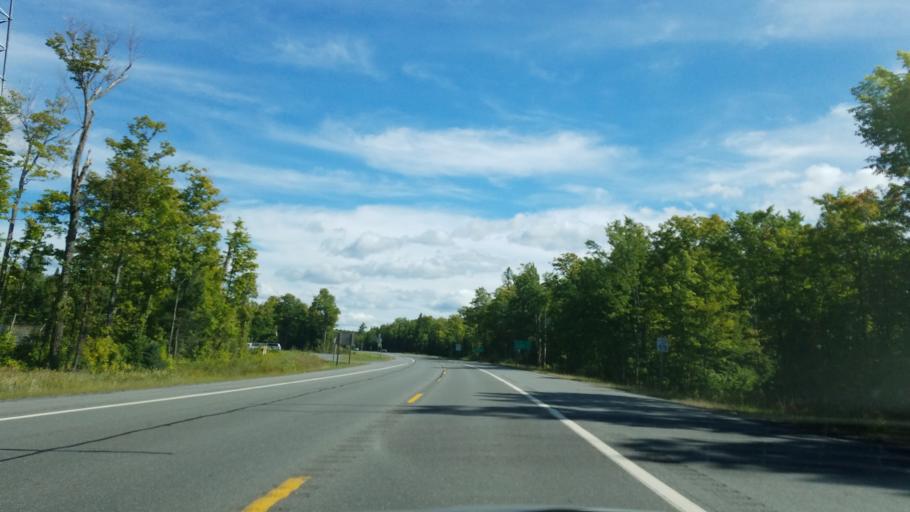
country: US
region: Michigan
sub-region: Baraga County
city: L'Anse
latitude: 46.5848
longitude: -88.4717
